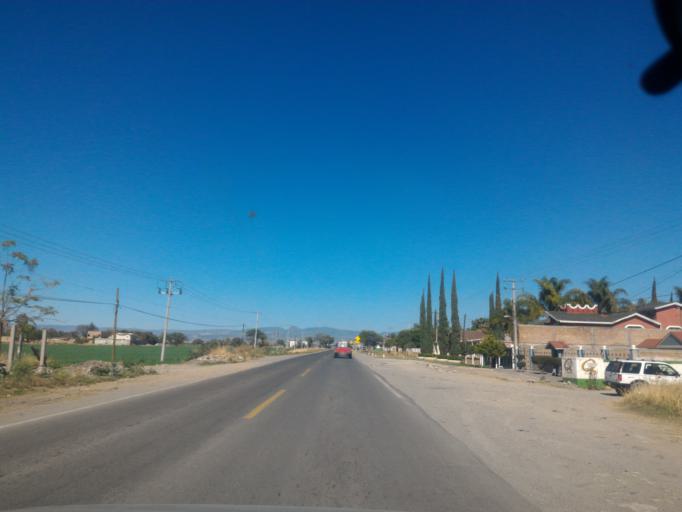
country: MX
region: Guanajuato
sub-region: Leon
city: Malagana (San Antonio del Monte)
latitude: 21.0478
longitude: -101.7555
